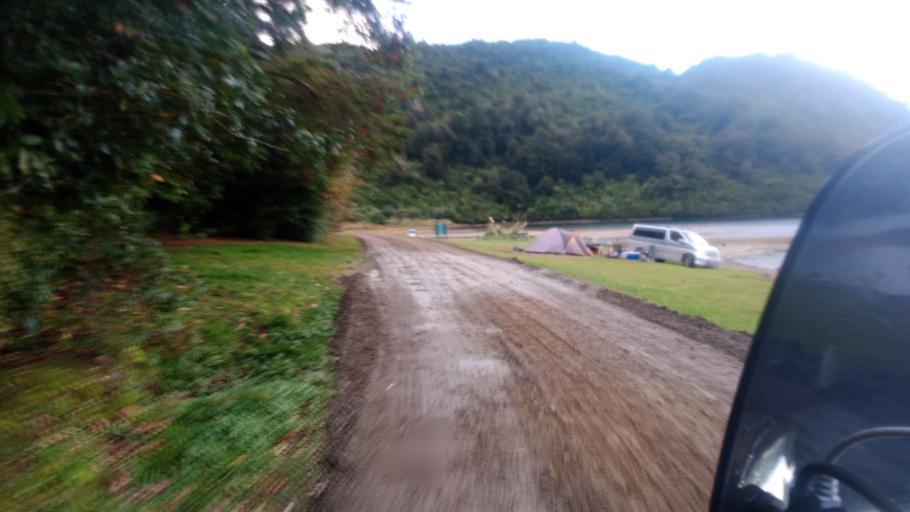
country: NZ
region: Hawke's Bay
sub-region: Wairoa District
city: Wairoa
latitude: -38.7329
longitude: 177.0880
